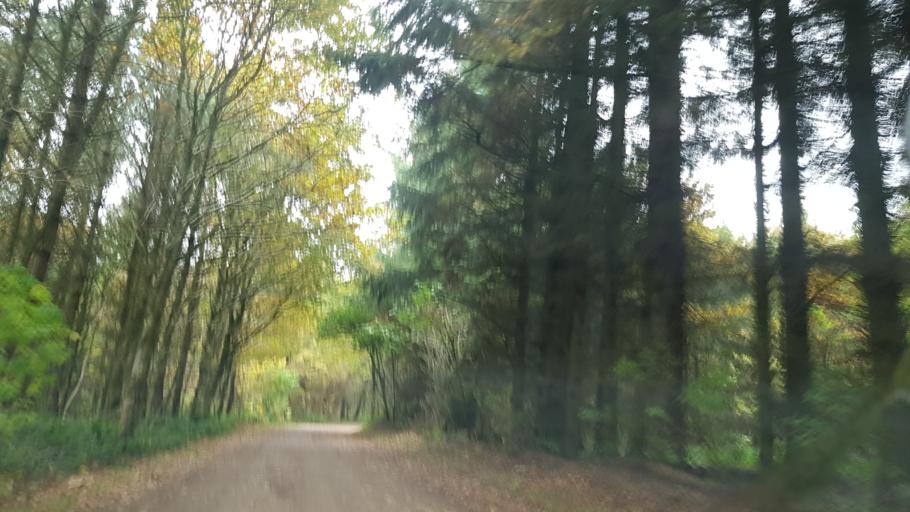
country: DK
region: South Denmark
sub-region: Tonder Kommune
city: Sherrebek
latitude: 55.1728
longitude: 8.7652
